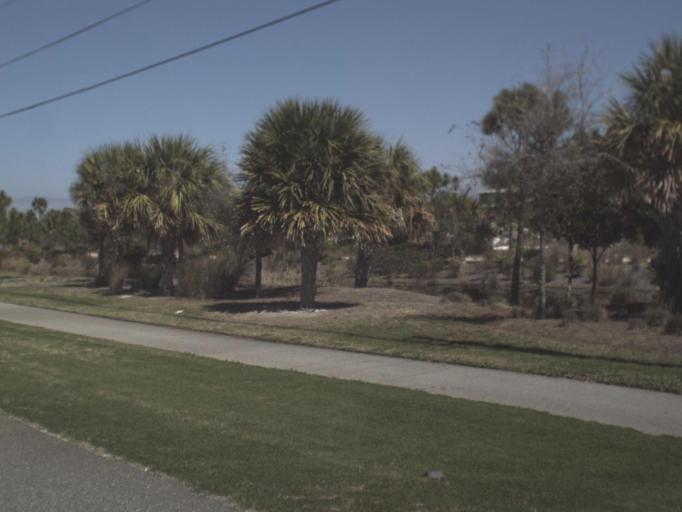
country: US
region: Florida
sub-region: Gulf County
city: Port Saint Joe
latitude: 29.7341
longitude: -85.3922
